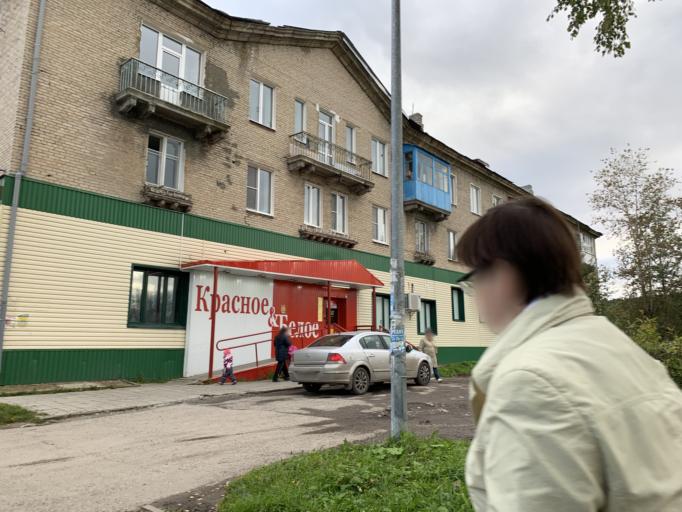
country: RU
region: Perm
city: Gubakha
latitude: 58.8457
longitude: 57.5482
